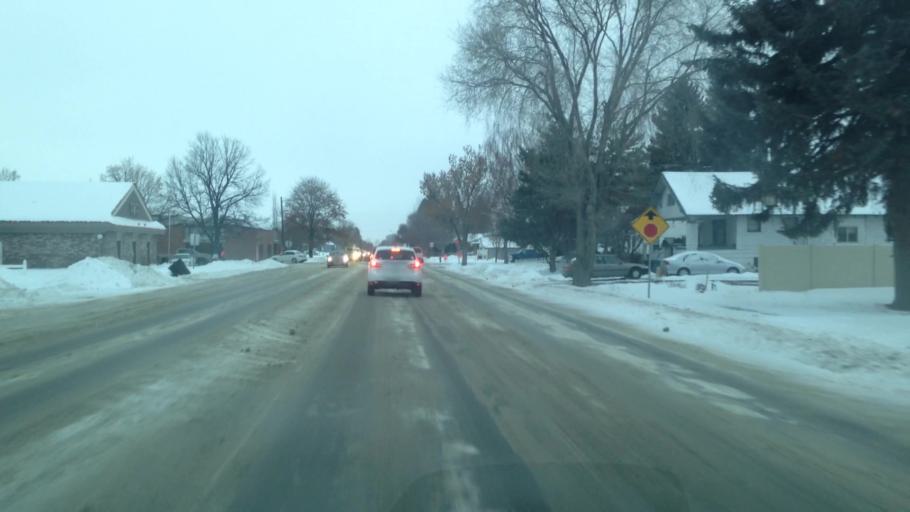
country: US
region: Idaho
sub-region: Madison County
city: Rexburg
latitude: 43.8282
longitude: -111.7823
